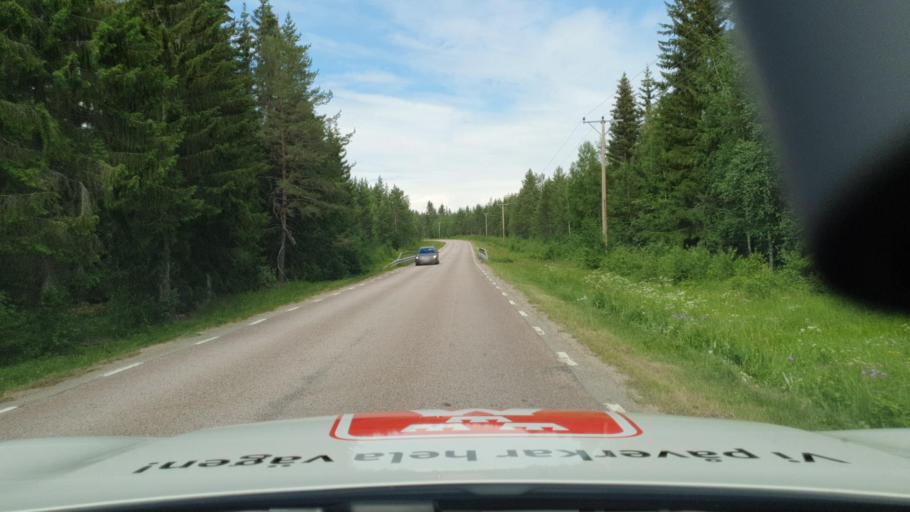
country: NO
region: Hedmark
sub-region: Grue
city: Kirkenaer
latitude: 60.7105
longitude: 12.6151
